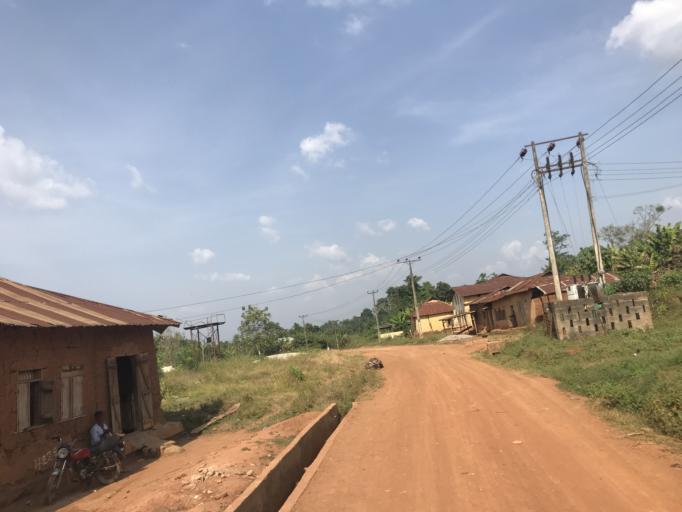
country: NG
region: Osun
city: Osu
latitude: 7.6518
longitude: 4.6652
